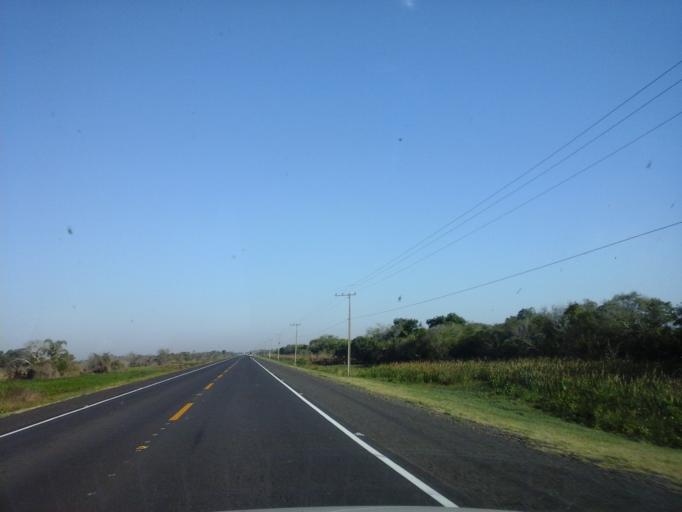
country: PY
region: Neembucu
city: Pilar
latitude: -26.8584
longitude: -58.1824
